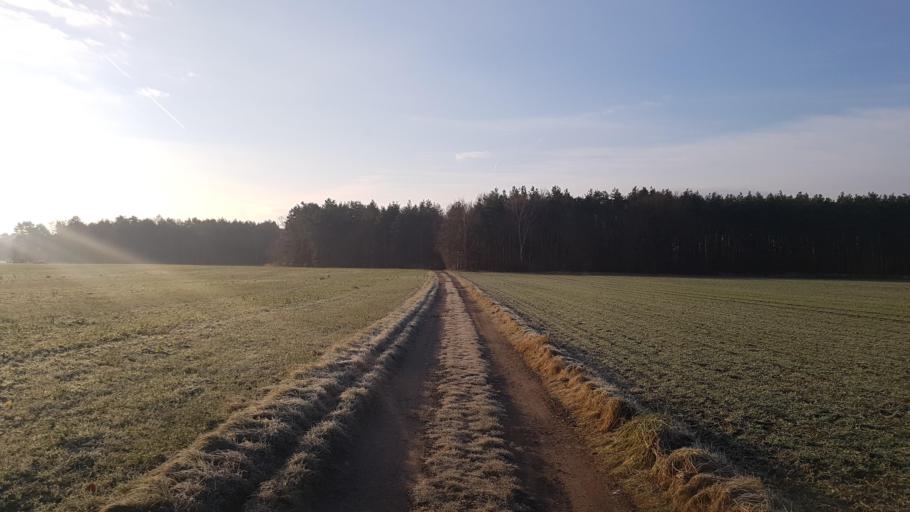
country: DE
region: Brandenburg
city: Plessa
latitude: 51.5304
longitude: 13.6184
